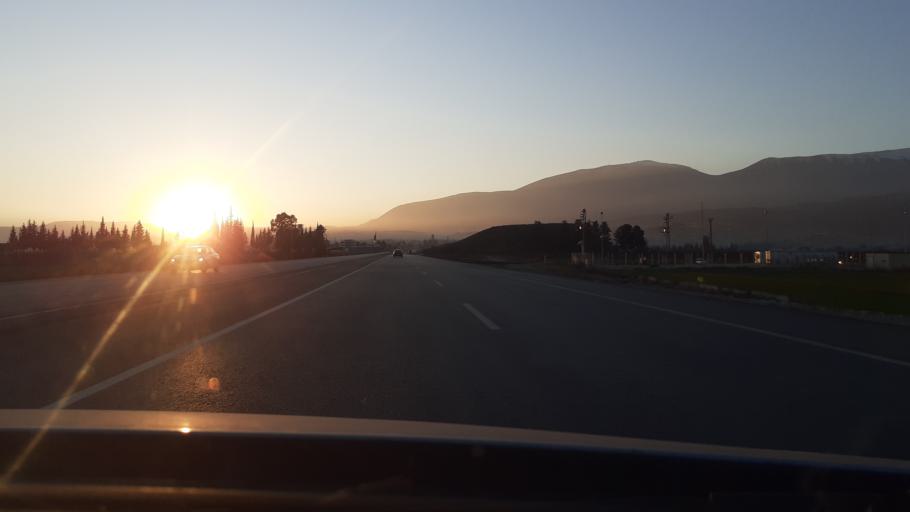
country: TR
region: Hatay
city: Kirikhan
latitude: 36.5032
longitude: 36.3980
